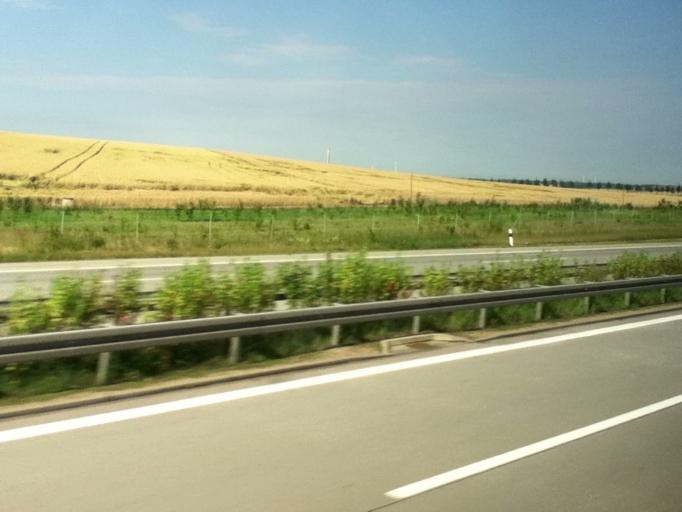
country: DE
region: Saxony
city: Remse
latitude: 50.8416
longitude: 12.5853
